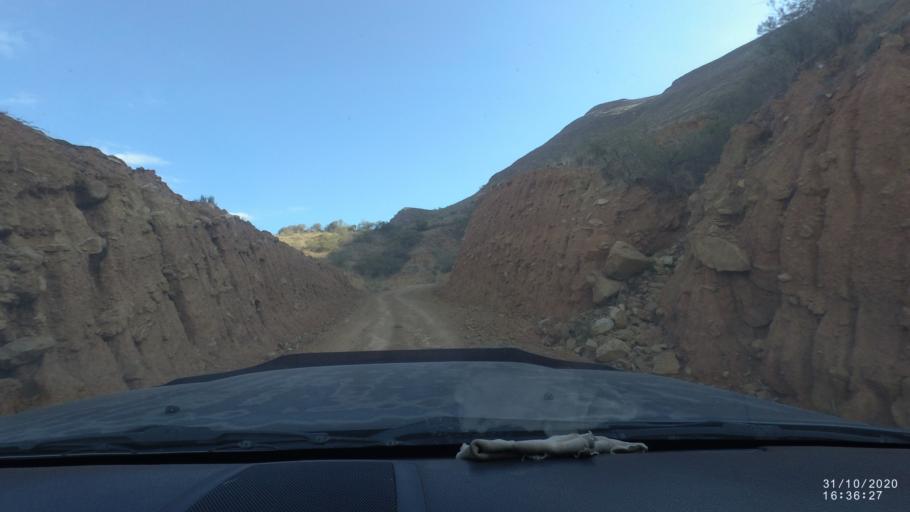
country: BO
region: Chuquisaca
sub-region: Provincia Zudanez
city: Mojocoya
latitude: -18.4596
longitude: -64.5827
